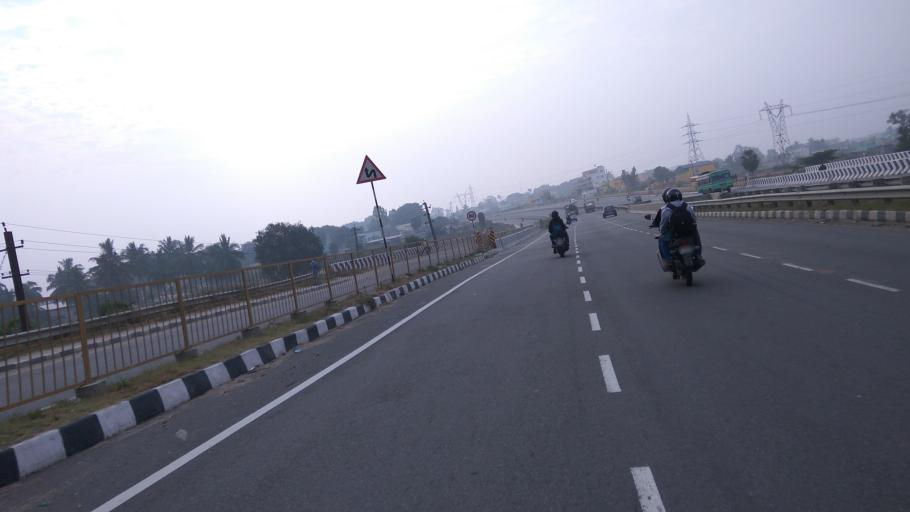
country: IN
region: Tamil Nadu
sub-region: Krishnagiri
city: Hosur
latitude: 12.7135
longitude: 77.8863
